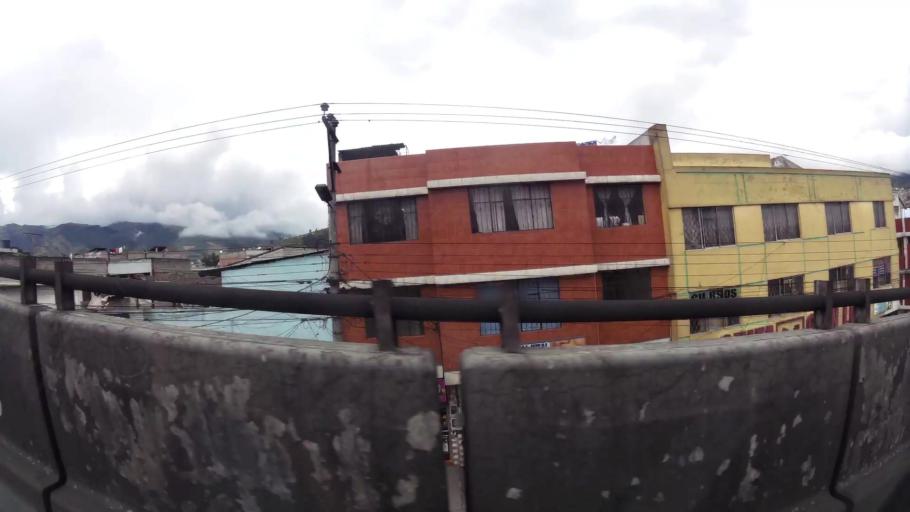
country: EC
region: Pichincha
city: Quito
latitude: -0.2781
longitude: -78.5526
